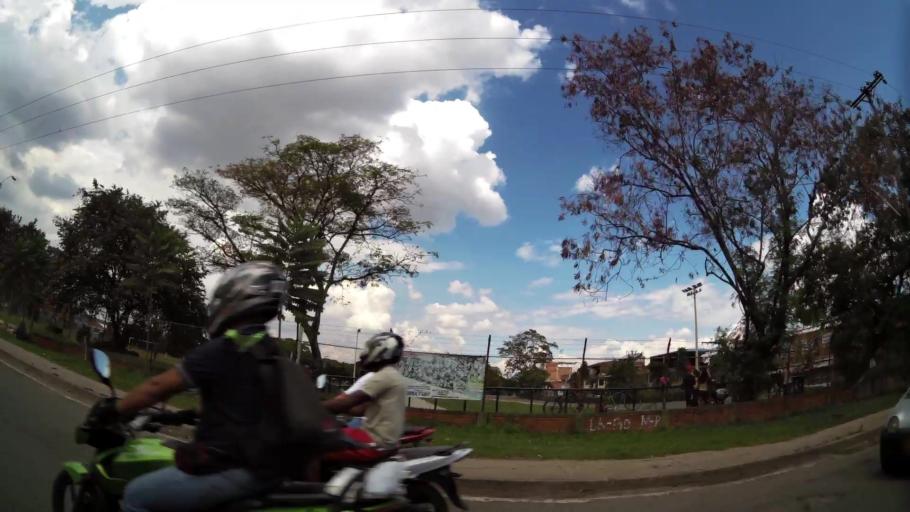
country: CO
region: Valle del Cauca
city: Cali
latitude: 3.4030
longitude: -76.5210
